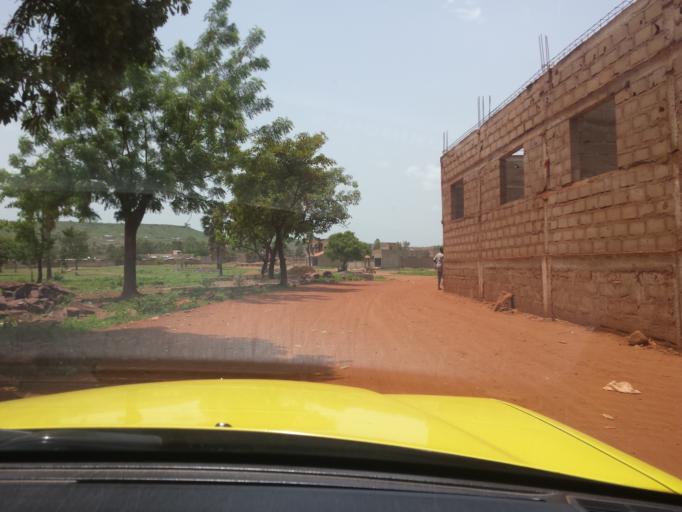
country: ML
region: Bamako
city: Bamako
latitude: 12.6104
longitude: -7.8882
